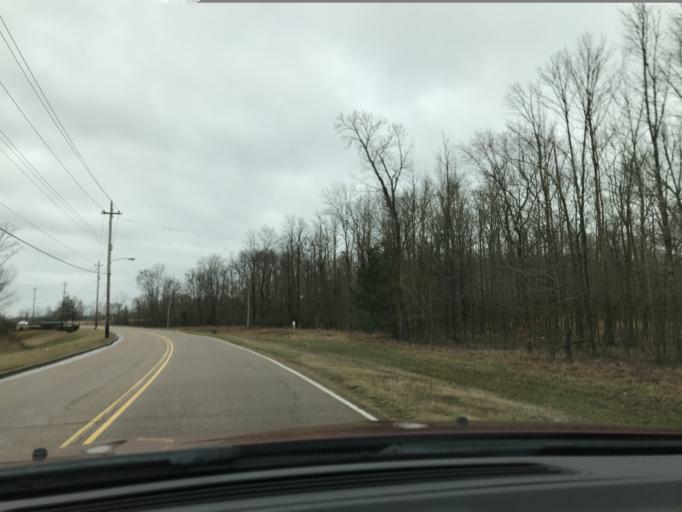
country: US
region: Tennessee
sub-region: Shelby County
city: Collierville
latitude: 35.0919
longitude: -89.7132
